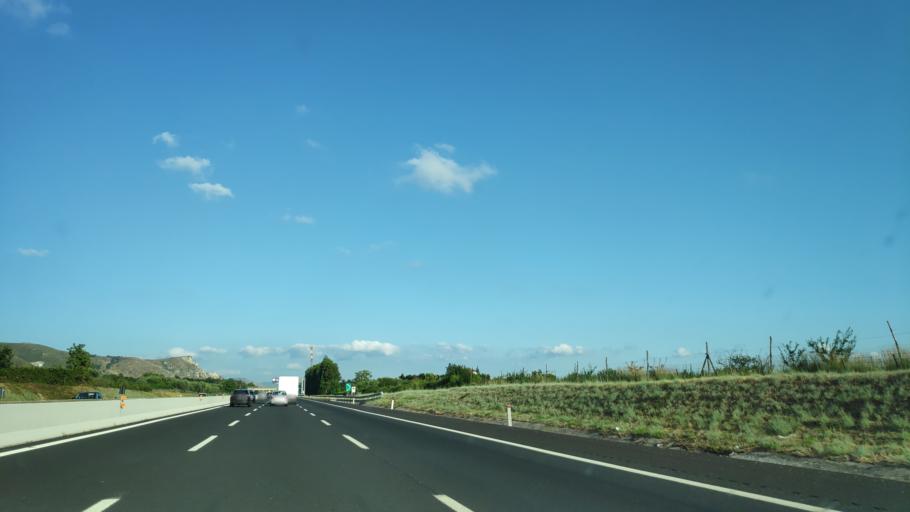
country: IT
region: Campania
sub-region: Provincia di Caserta
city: Sant'Angelo in Formis
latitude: 41.1118
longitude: 14.2406
